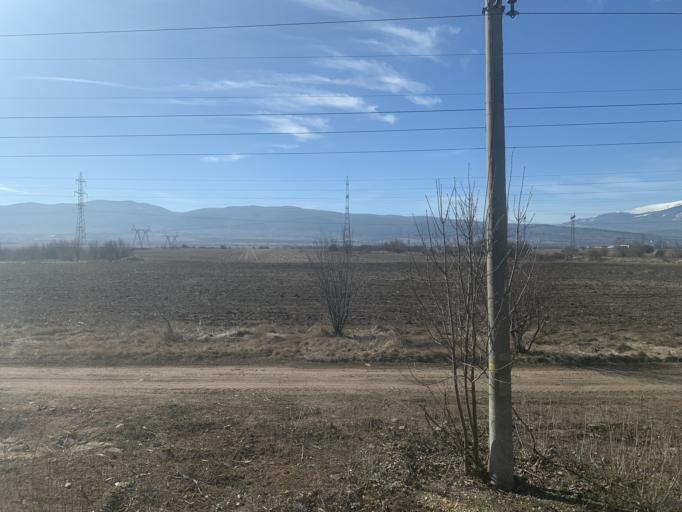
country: BG
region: Sofiya
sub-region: Obshtina Elin Pelin
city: Elin Pelin
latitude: 42.6498
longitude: 23.4810
